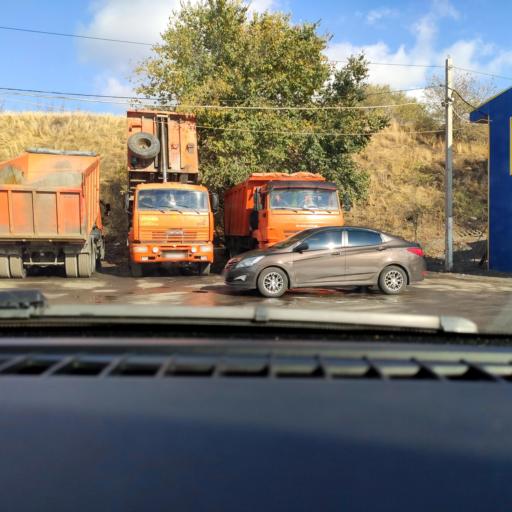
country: RU
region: Voronezj
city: Maslovka
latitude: 51.6253
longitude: 39.2595
